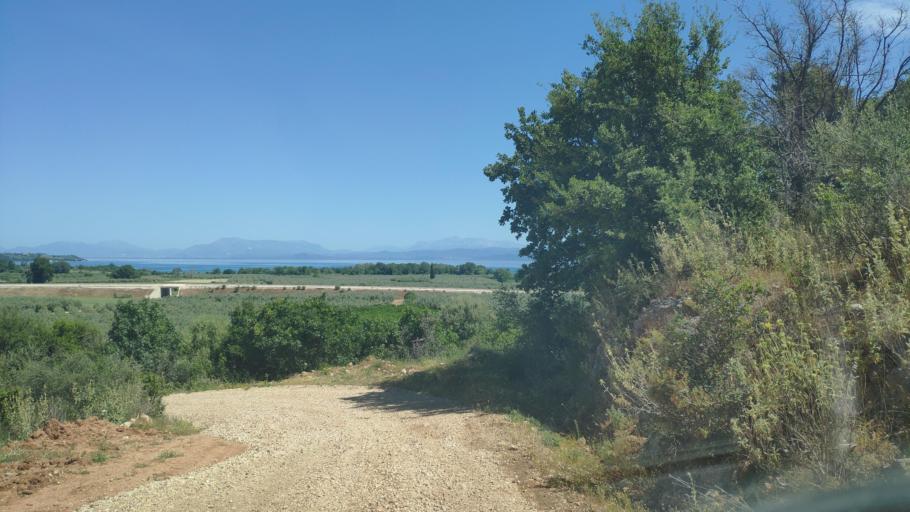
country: GR
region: West Greece
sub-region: Nomos Aitolias kai Akarnanias
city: Monastirakion
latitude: 38.8691
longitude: 21.0526
